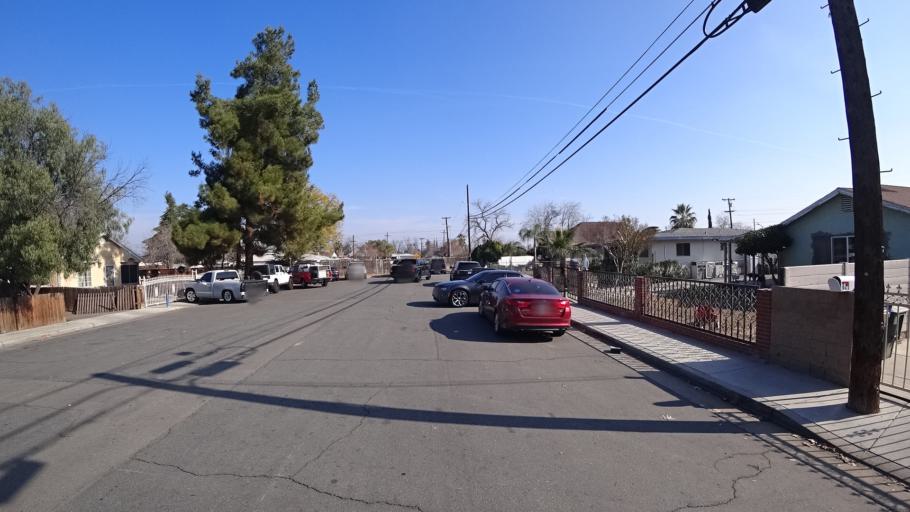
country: US
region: California
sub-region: Kern County
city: Bakersfield
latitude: 35.3627
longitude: -119.0089
